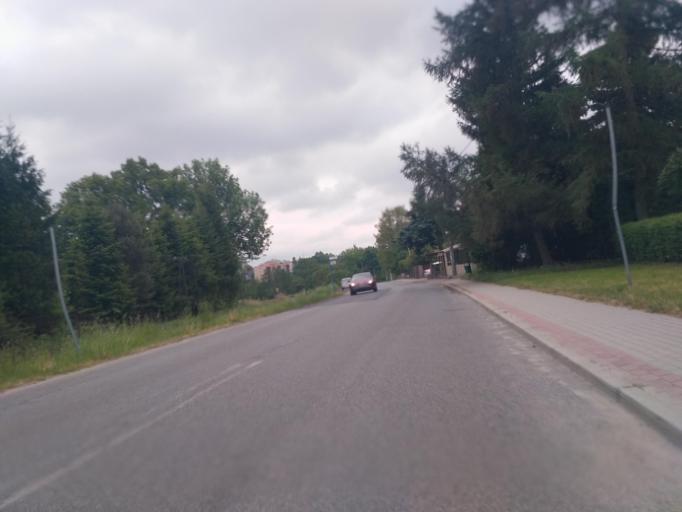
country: PL
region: Subcarpathian Voivodeship
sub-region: Krosno
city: Krosno
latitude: 49.6883
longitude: 21.7596
